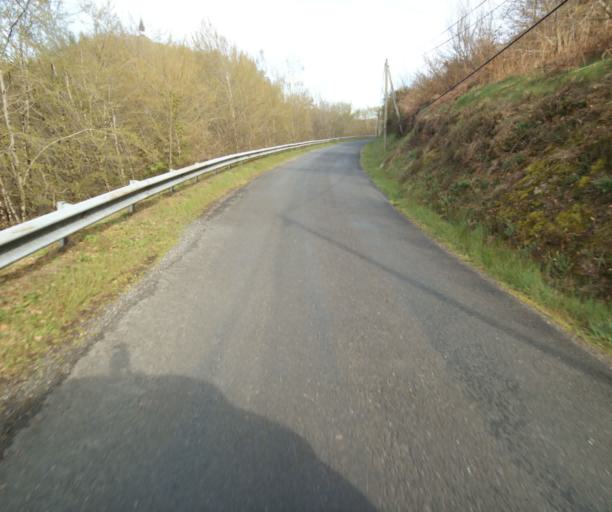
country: FR
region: Limousin
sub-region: Departement de la Correze
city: Naves
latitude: 45.3445
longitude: 1.8190
